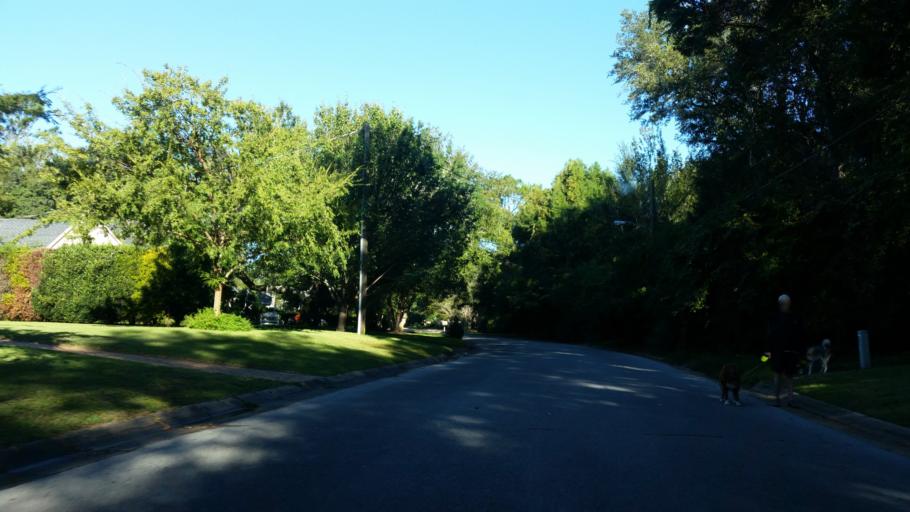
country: US
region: Florida
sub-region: Escambia County
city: East Pensacola Heights
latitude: 30.4685
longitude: -87.1676
